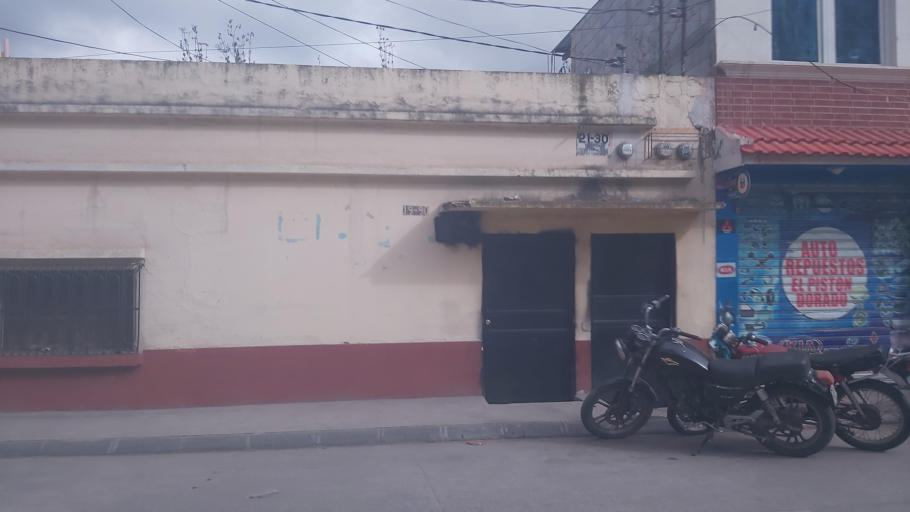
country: GT
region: Quetzaltenango
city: Quetzaltenango
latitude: 14.8290
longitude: -91.5274
